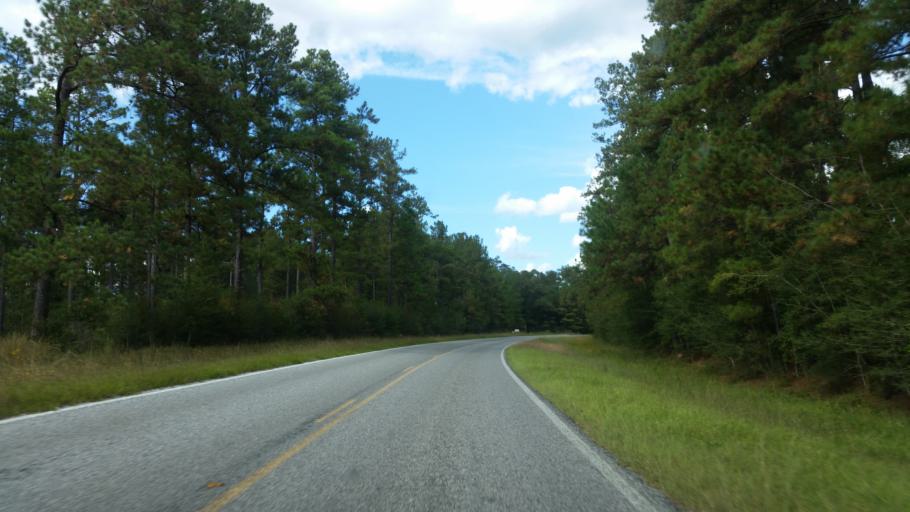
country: US
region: Mississippi
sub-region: Stone County
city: Wiggins
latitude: 30.9775
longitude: -89.0569
